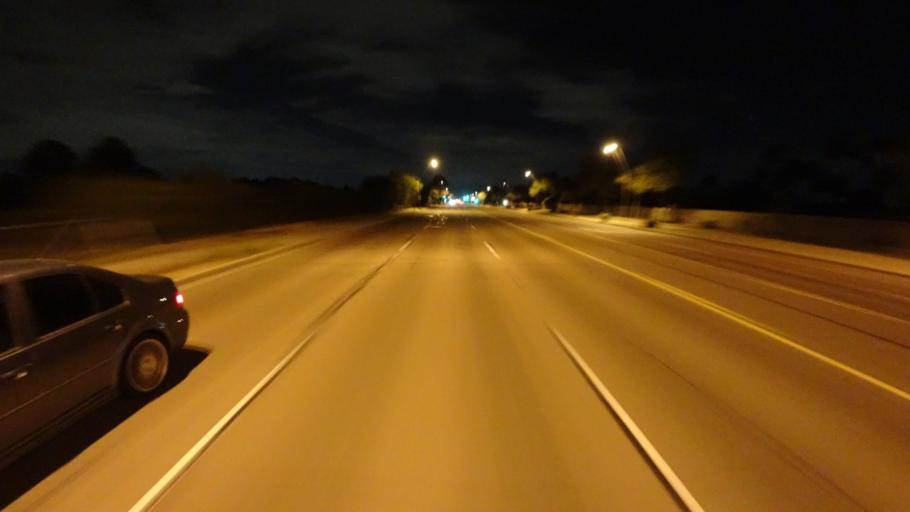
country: US
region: Arizona
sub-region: Maricopa County
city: Guadalupe
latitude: 33.3388
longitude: -111.9286
